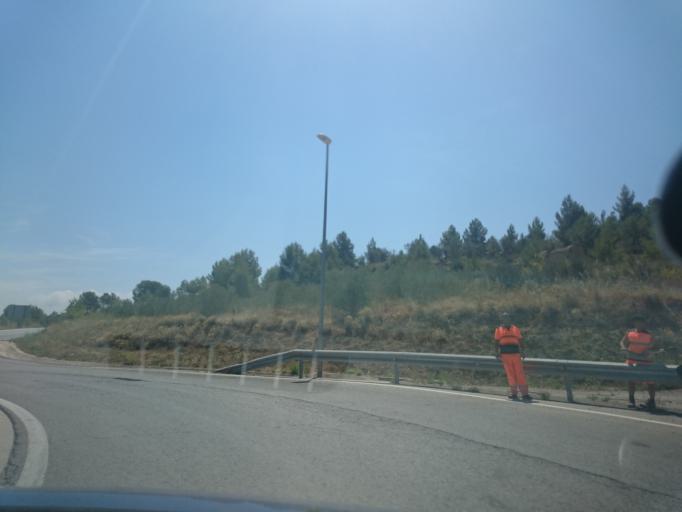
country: ES
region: Catalonia
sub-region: Provincia de Barcelona
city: Sant Pere de Riudebitlles
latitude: 41.4546
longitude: 1.6800
